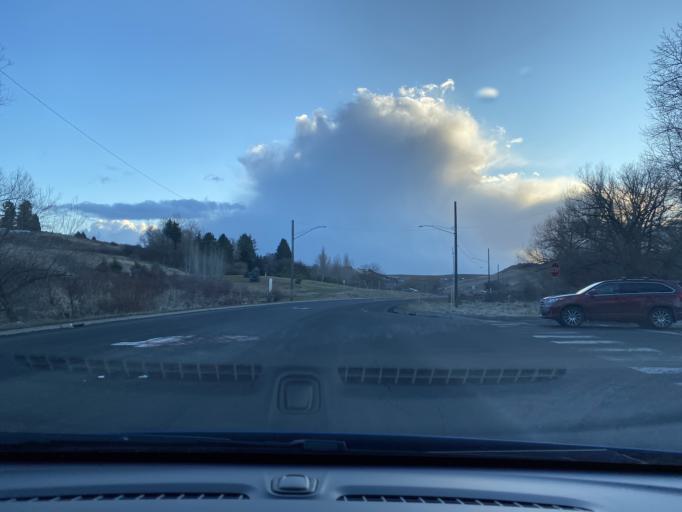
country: US
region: Washington
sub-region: Whitman County
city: Pullman
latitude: 46.7291
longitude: -117.1390
